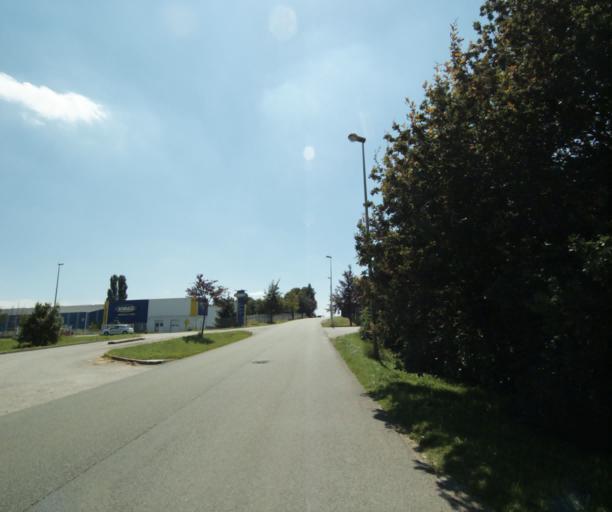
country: FR
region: Pays de la Loire
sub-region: Departement de la Mayenne
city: Laval
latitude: 48.0890
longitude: -0.7373
